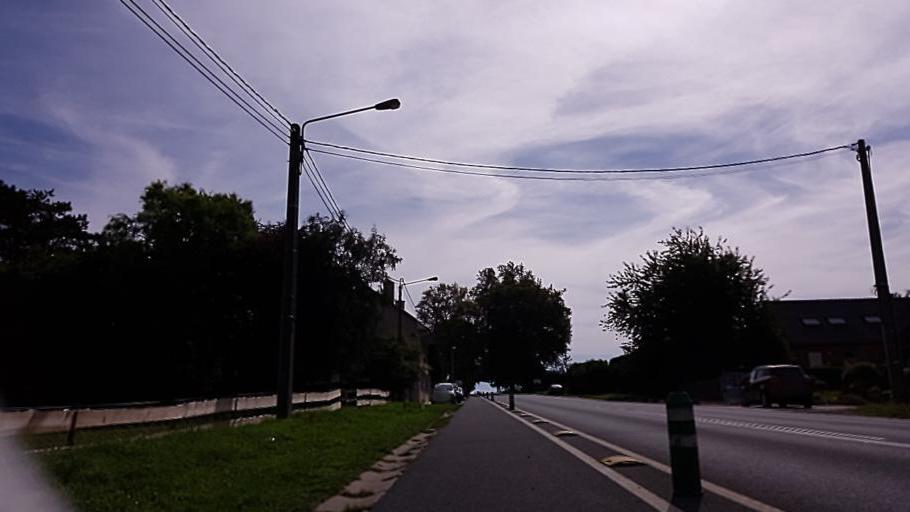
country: BE
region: Wallonia
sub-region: Province du Brabant Wallon
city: Grez-Doiceau
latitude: 50.7736
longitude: 4.7230
